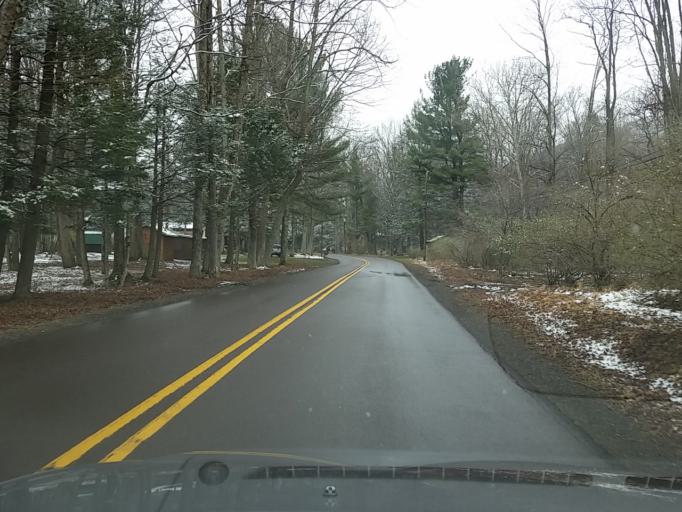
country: US
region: Pennsylvania
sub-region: Sullivan County
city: Laporte
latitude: 41.3013
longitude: -76.3915
